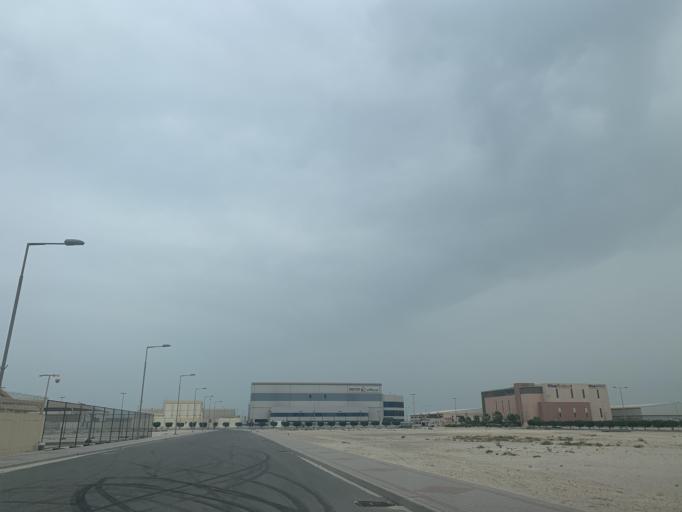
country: BH
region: Muharraq
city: Al Hadd
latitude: 26.2142
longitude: 50.6773
